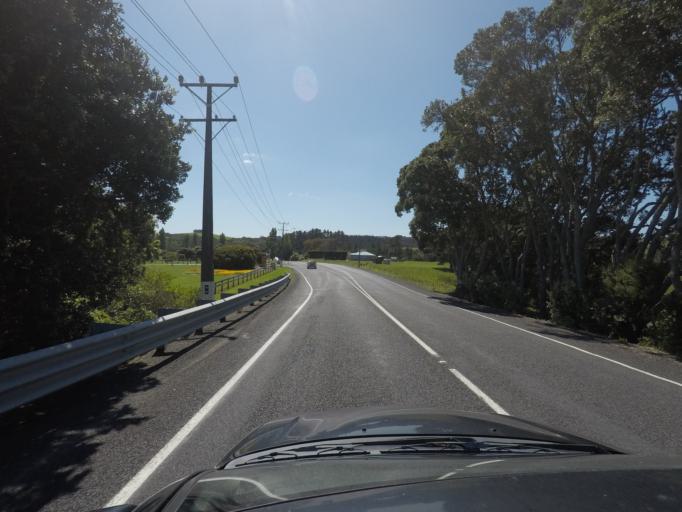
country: NZ
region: Auckland
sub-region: Auckland
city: Pakuranga
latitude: -36.8855
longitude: 175.0159
